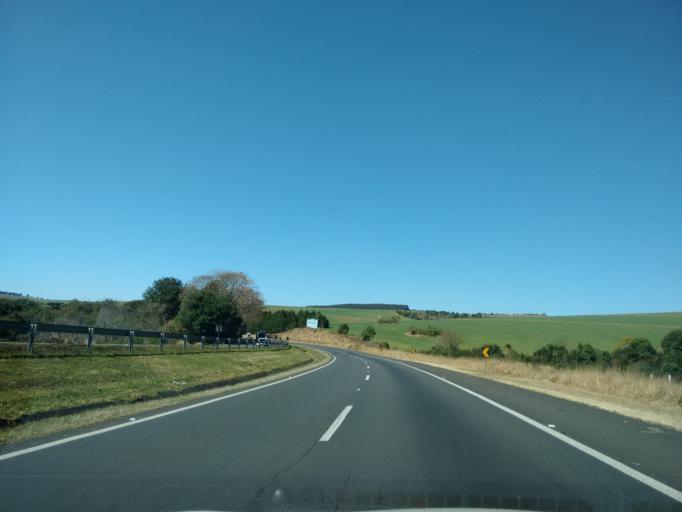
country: BR
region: Parana
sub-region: Palmeira
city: Palmeira
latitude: -25.2667
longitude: -49.9701
